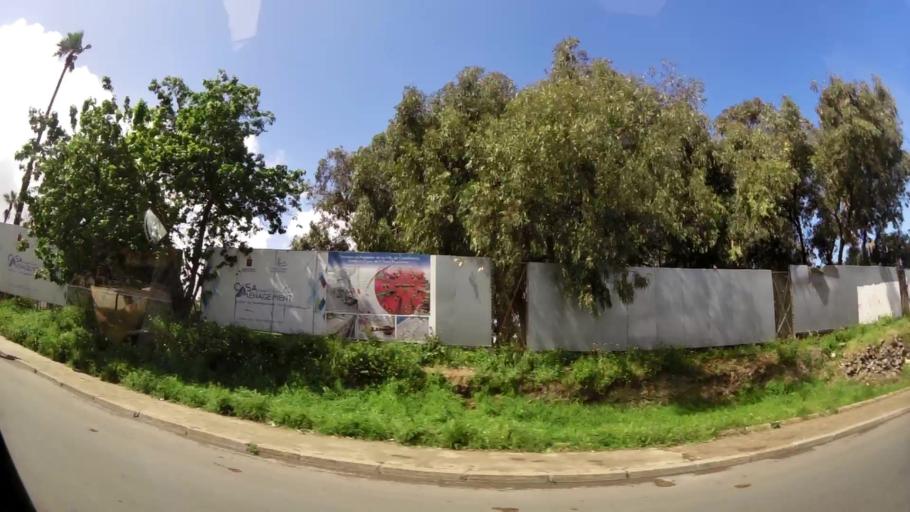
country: MA
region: Grand Casablanca
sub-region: Mediouna
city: Tit Mellil
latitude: 33.6061
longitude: -7.5281
